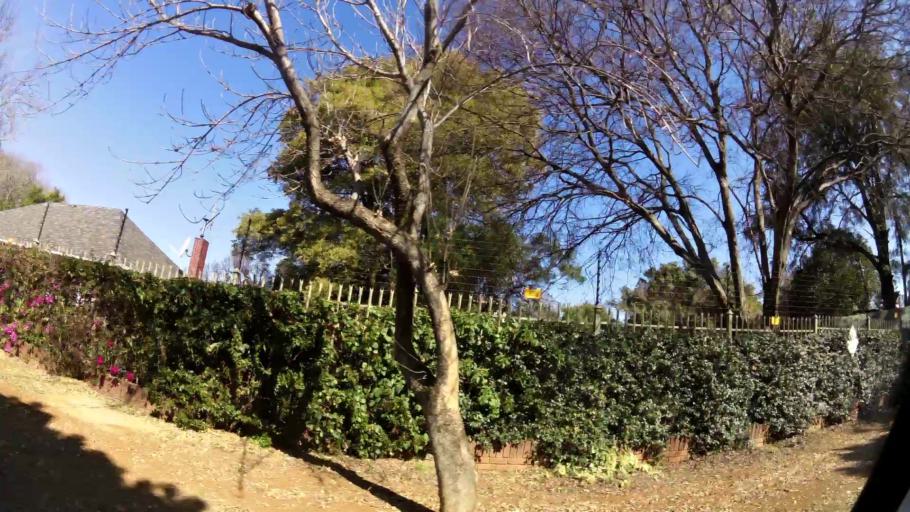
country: ZA
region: Gauteng
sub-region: City of Tshwane Metropolitan Municipality
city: Pretoria
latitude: -25.7624
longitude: 28.2496
